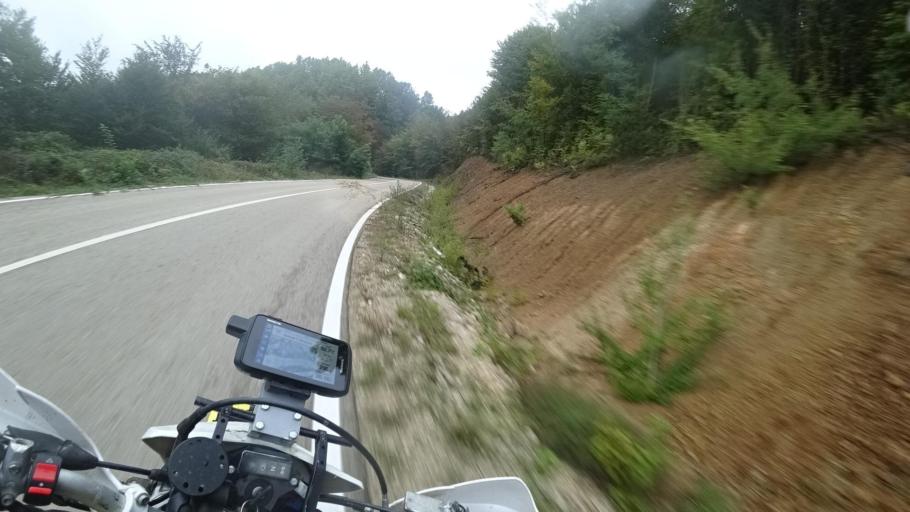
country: BA
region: Republika Srpska
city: Maricka
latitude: 44.8059
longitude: 16.8412
